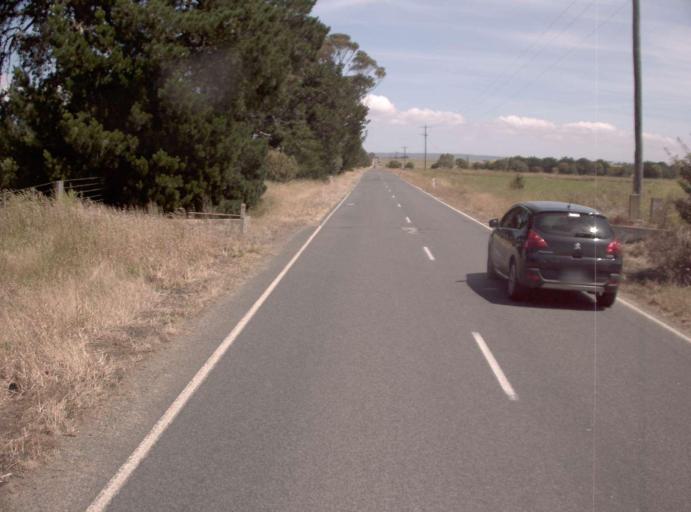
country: AU
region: Victoria
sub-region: Wellington
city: Heyfield
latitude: -38.0933
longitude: 146.8659
